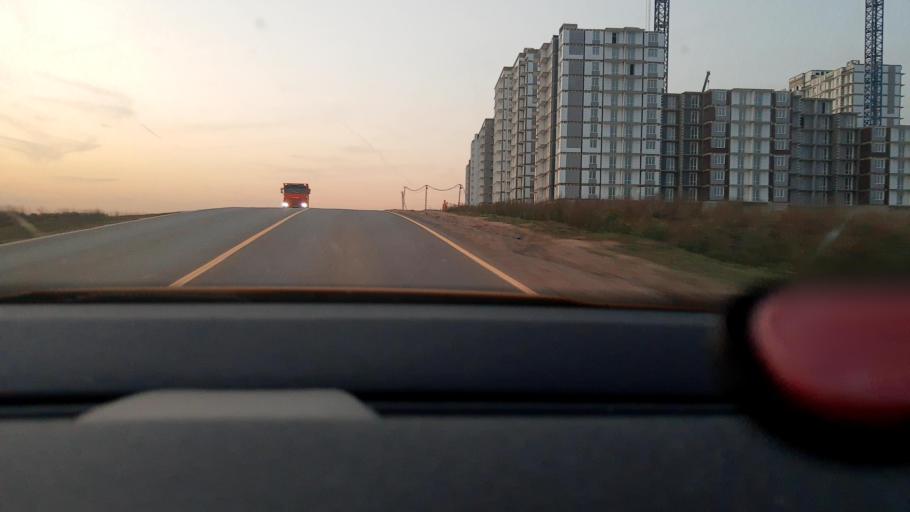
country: RU
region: Moskovskaya
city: Filimonki
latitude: 55.5303
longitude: 37.3789
